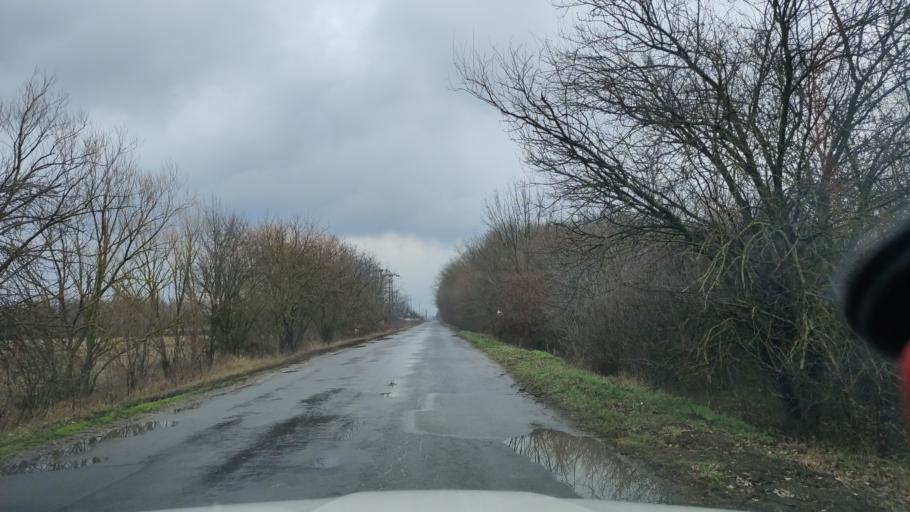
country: HU
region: Hajdu-Bihar
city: Hajduszoboszlo
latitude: 47.4624
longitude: 21.4061
